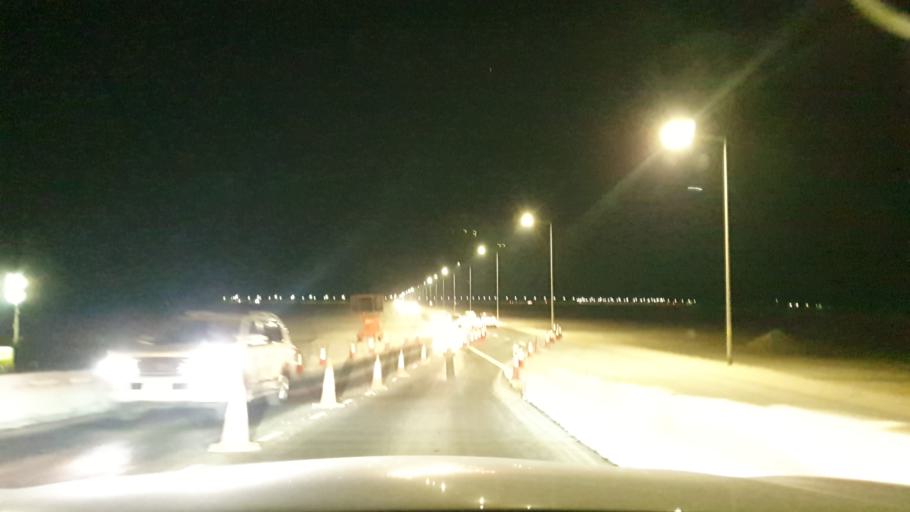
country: BH
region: Muharraq
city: Al Muharraq
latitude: 26.2807
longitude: 50.5898
